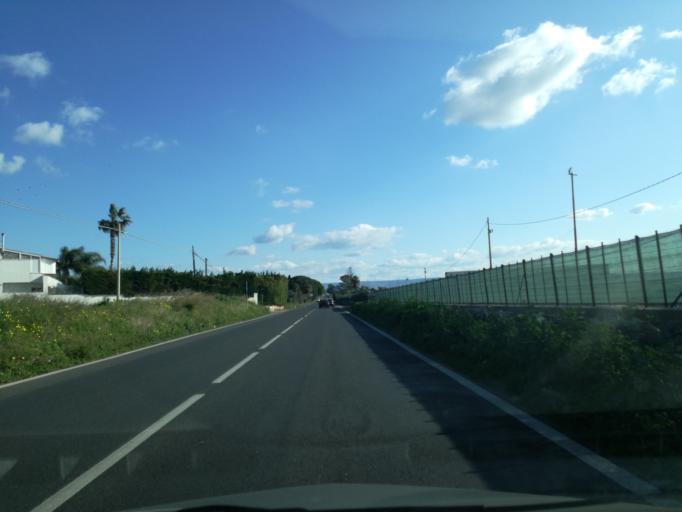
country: IT
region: Sicily
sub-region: Ragusa
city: Vittoria
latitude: 36.9616
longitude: 14.4948
